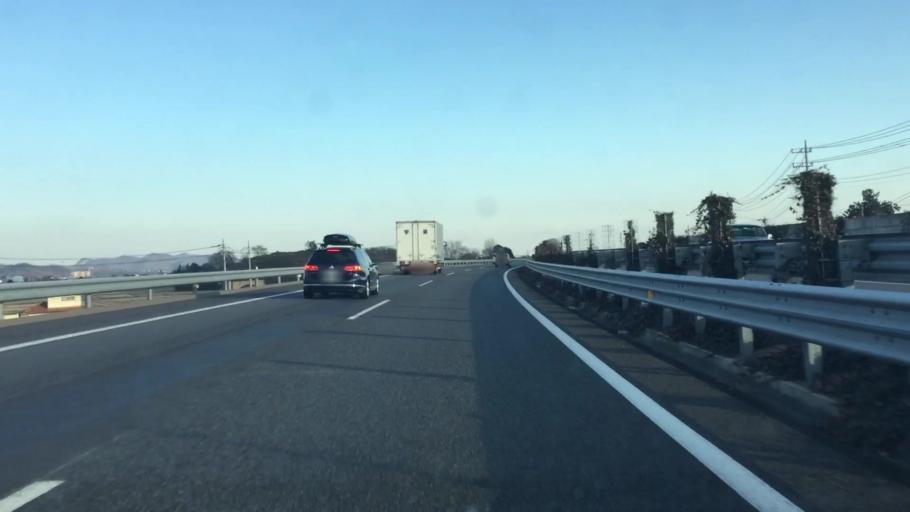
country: JP
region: Gunma
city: Ota
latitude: 36.3362
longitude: 139.3684
